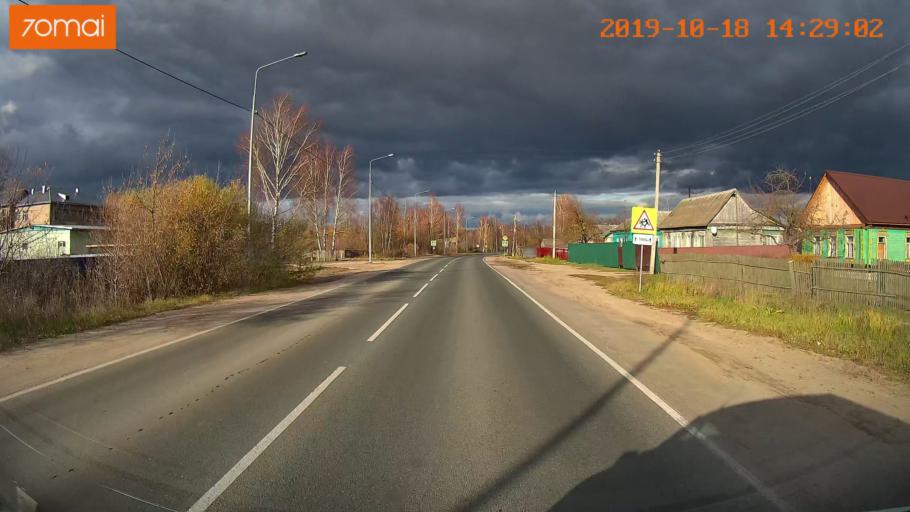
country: RU
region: Rjazan
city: Tuma
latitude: 55.1535
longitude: 40.5552
